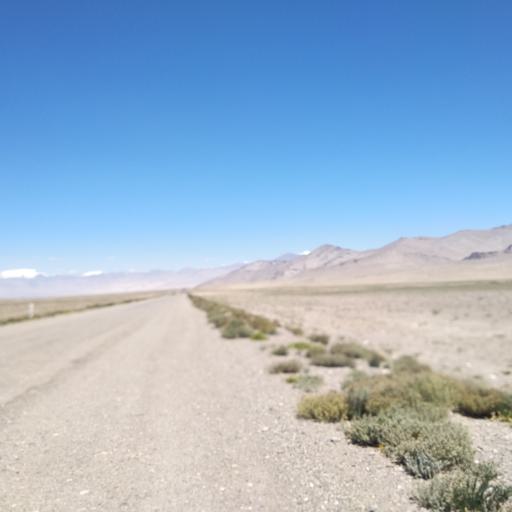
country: TJ
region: Gorno-Badakhshan
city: Murghob
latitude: 38.8987
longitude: 73.4967
